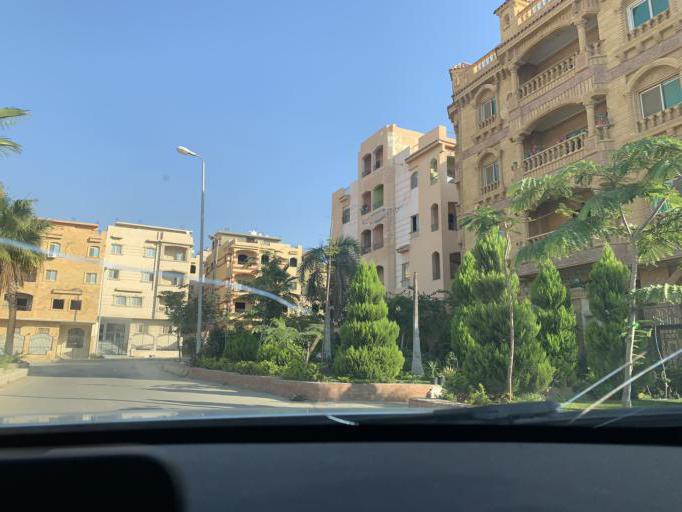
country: EG
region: Muhafazat al Qalyubiyah
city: Al Khankah
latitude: 30.0020
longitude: 31.4840
